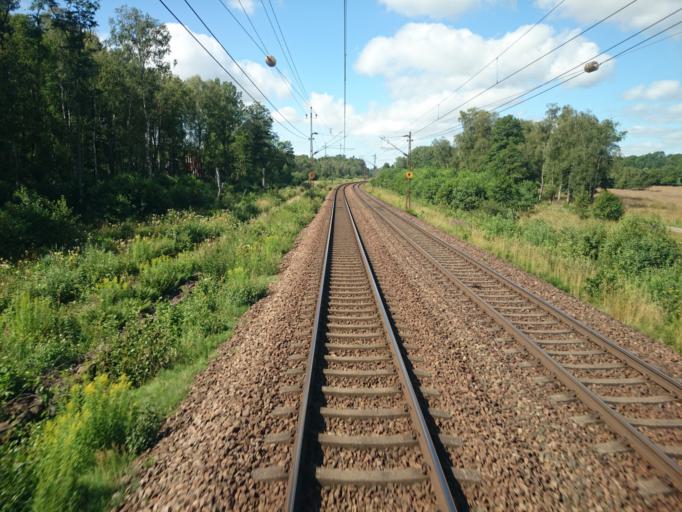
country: SE
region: Skane
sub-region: Hoors Kommun
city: Hoeoer
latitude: 55.9290
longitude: 13.5234
